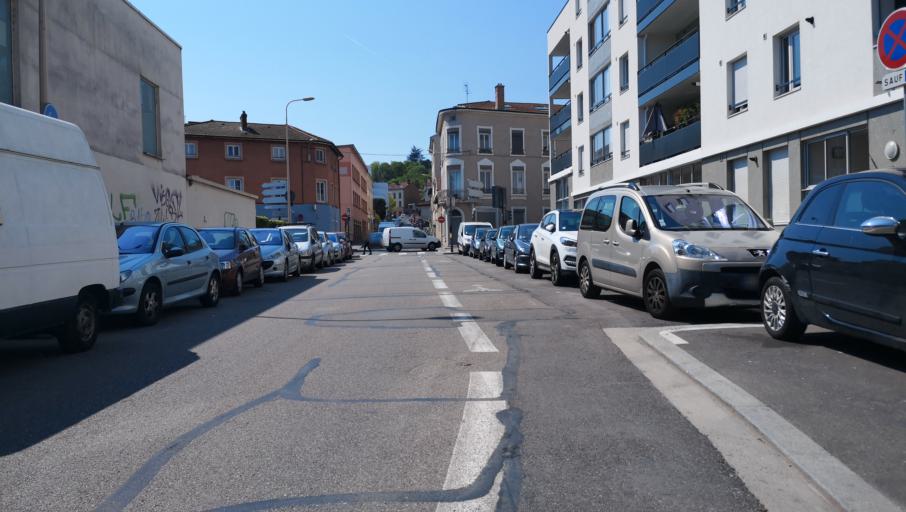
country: FR
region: Rhone-Alpes
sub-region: Departement du Rhone
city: Tassin-la-Demi-Lune
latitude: 45.7736
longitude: 4.7960
